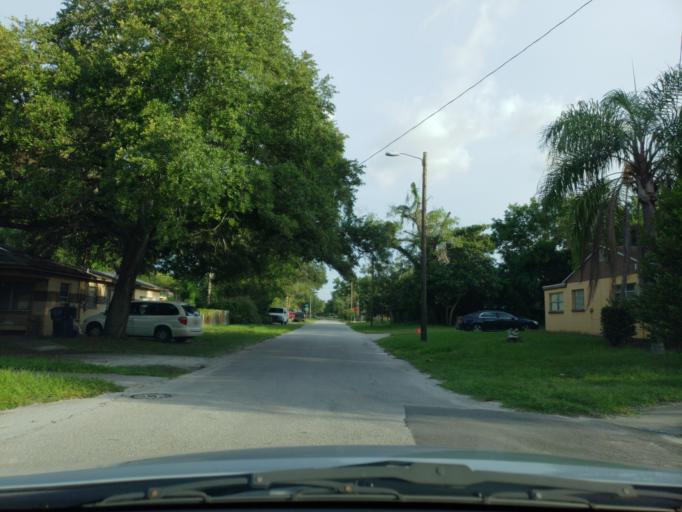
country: US
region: Florida
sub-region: Hillsborough County
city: Tampa
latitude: 27.9805
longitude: -82.4415
